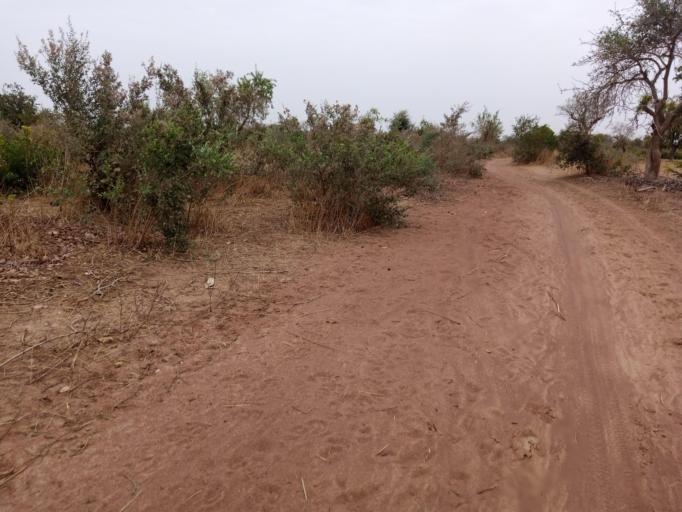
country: BF
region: Boucle du Mouhoun
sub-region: Province de la Kossi
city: Nouna
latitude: 12.8455
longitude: -4.0778
